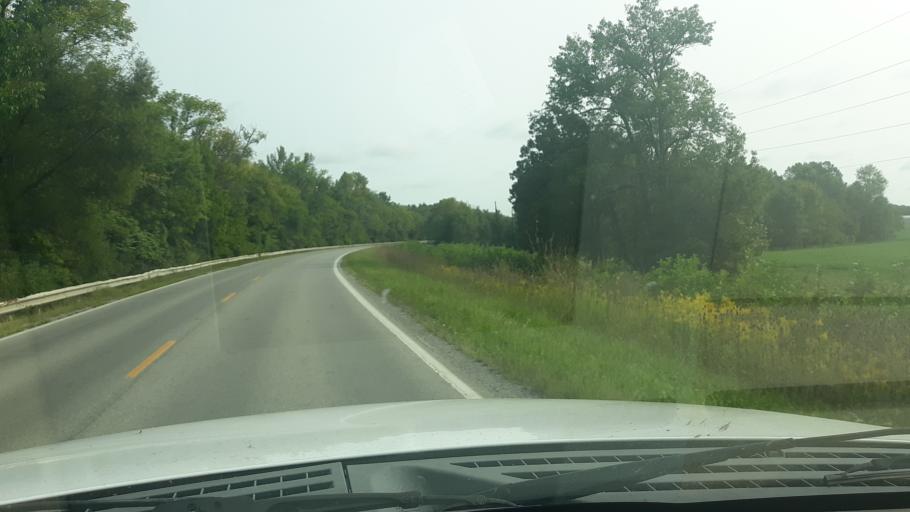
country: US
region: Illinois
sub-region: Saline County
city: Eldorado
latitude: 37.8908
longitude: -88.3829
